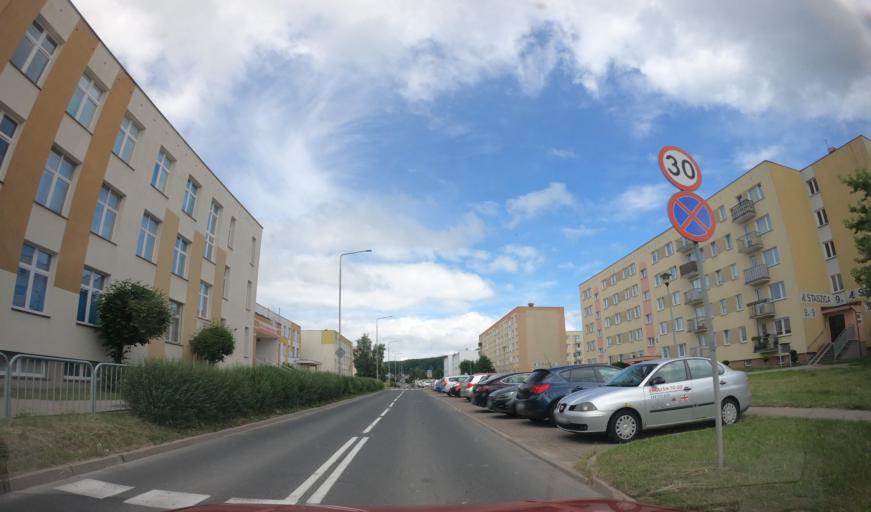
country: PL
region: West Pomeranian Voivodeship
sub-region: Koszalin
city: Koszalin
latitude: 54.2107
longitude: 16.1985
